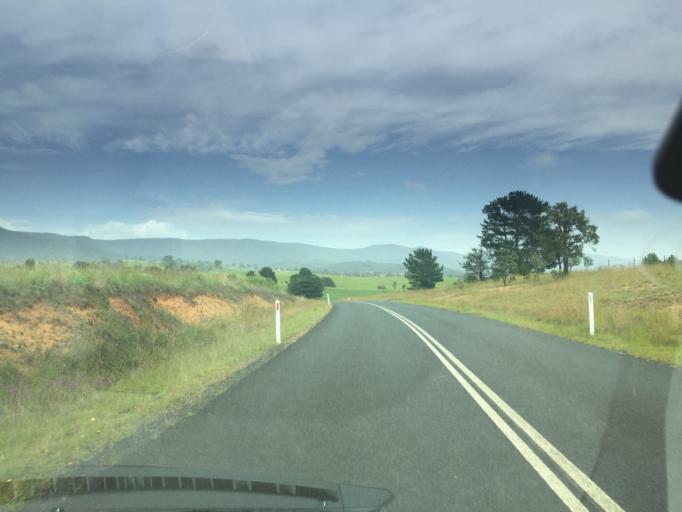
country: AU
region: New South Wales
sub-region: Bega Valley
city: Bega
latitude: -36.7288
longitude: 149.6280
